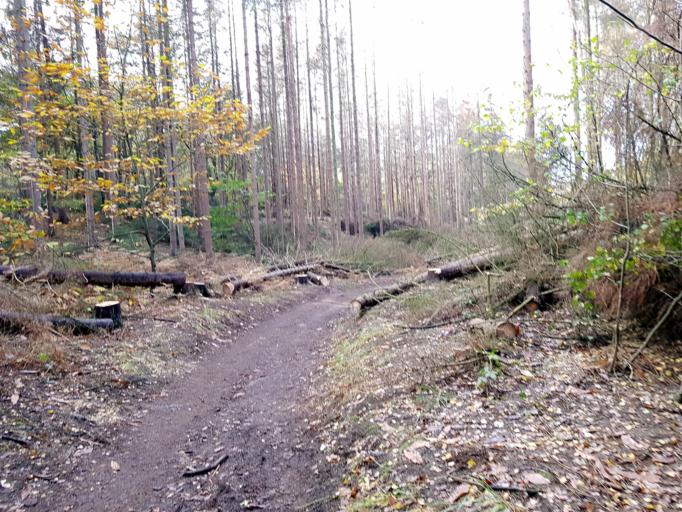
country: NL
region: Gelderland
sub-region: Gemeente Groesbeek
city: Bredeweg
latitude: 51.7469
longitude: 5.9165
